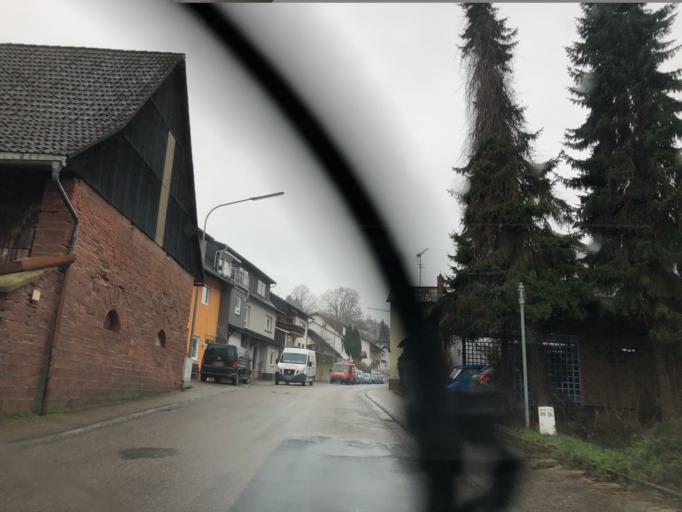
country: DE
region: Hesse
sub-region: Regierungsbezirk Darmstadt
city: Lutzelbach
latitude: 49.7696
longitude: 9.1051
